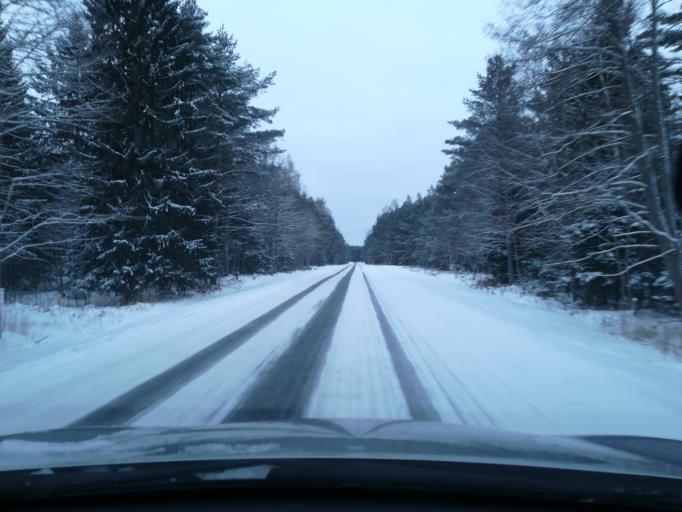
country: EE
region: Harju
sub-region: Keila linn
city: Keila
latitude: 59.3865
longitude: 24.2974
